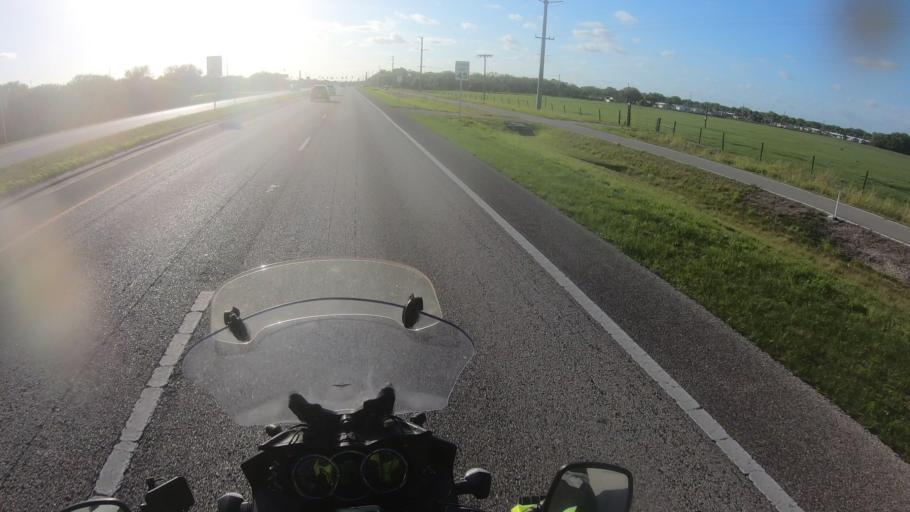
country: US
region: Florida
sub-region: DeSoto County
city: Arcadia
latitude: 27.2086
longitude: -81.8262
